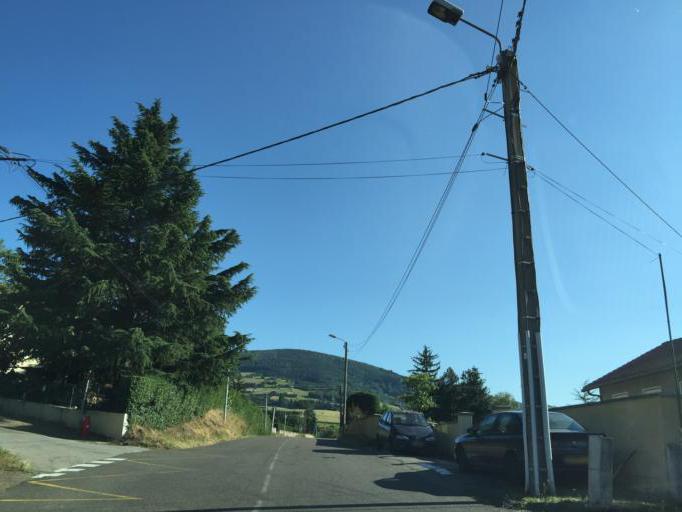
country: FR
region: Rhone-Alpes
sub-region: Departement de la Loire
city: Saint-Jean-Bonnefonds
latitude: 45.4530
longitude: 4.4858
